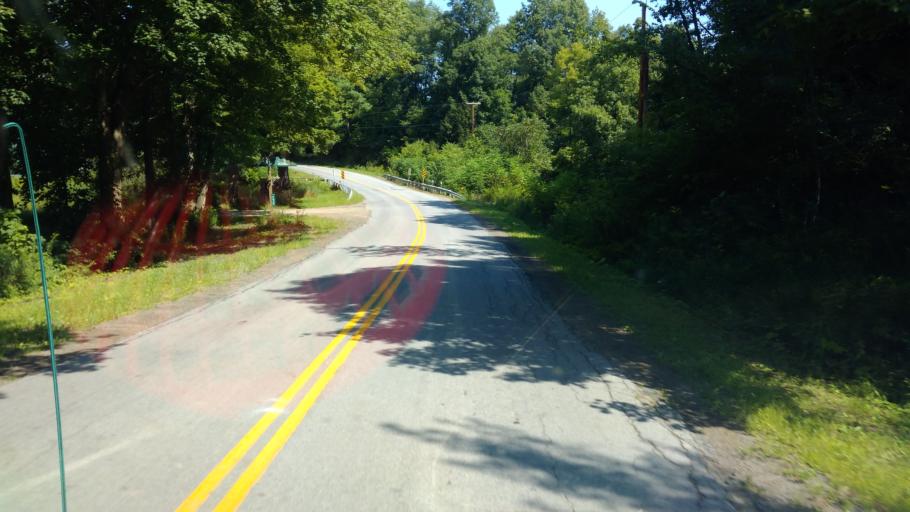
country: US
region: New York
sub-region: Allegany County
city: Belmont
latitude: 42.2878
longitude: -78.0530
